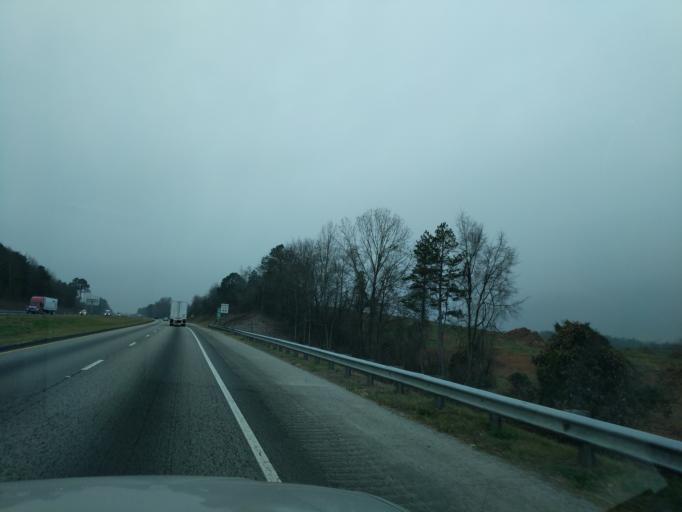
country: US
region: Georgia
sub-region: Jackson County
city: Commerce
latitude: 34.2493
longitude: -83.4734
